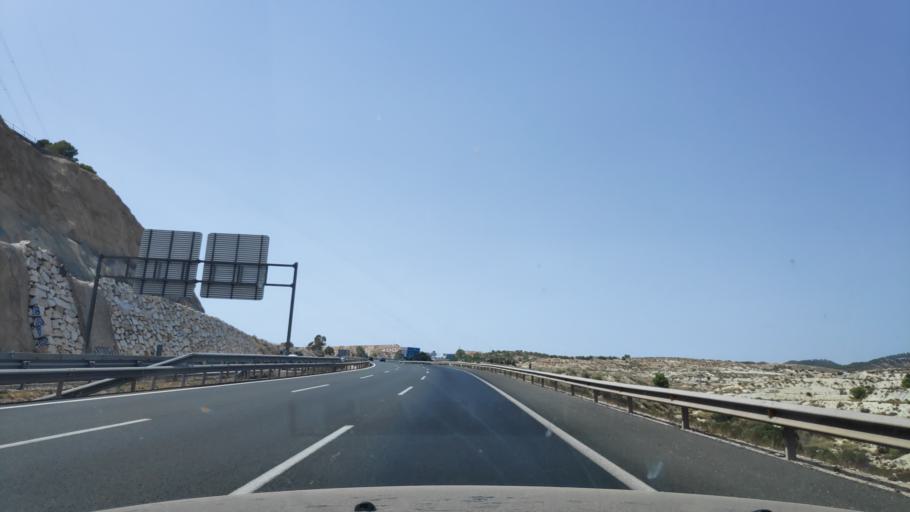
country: ES
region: Murcia
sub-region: Murcia
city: Murcia
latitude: 37.8739
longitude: -1.1271
